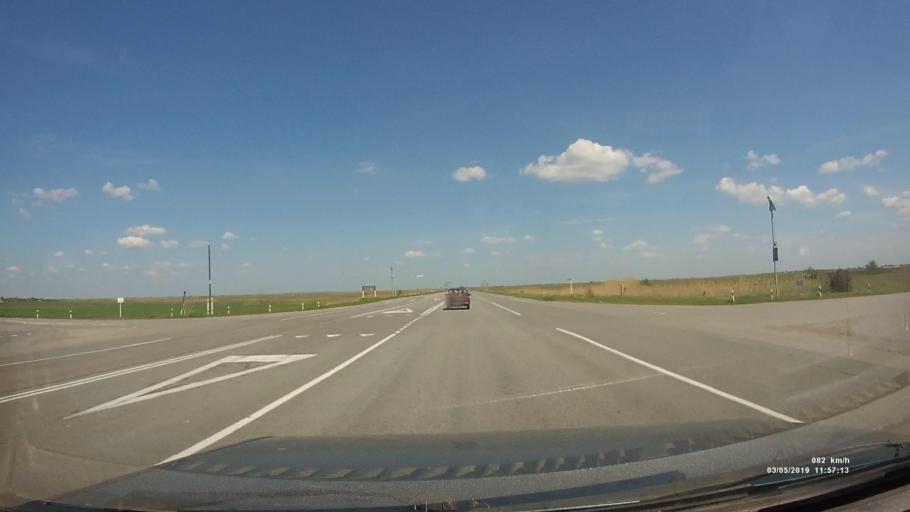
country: RU
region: Rostov
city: Bagayevskaya
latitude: 47.2039
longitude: 40.3078
